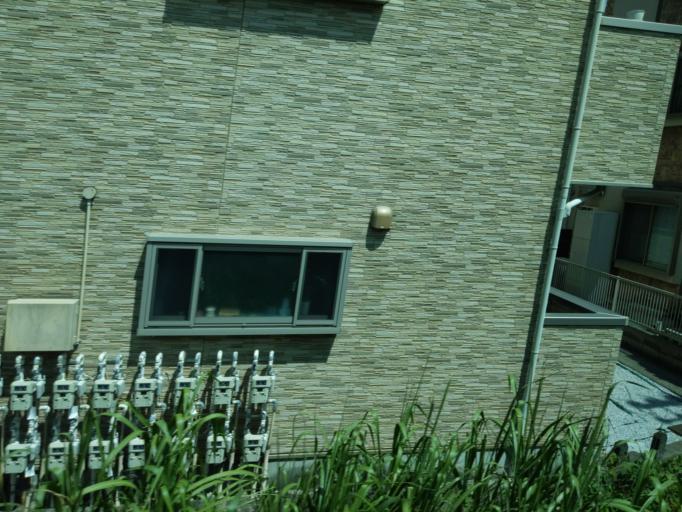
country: JP
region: Tokyo
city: Chofugaoka
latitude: 35.6299
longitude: 139.5517
